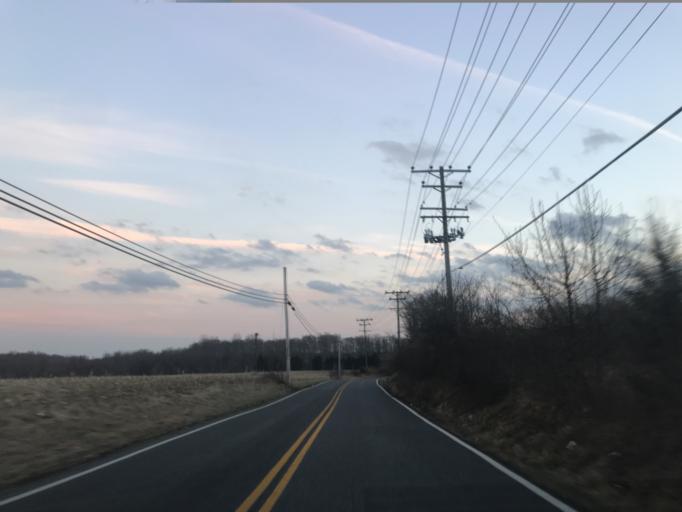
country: US
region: Maryland
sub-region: Harford County
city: South Bel Air
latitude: 39.5531
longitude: -76.2866
